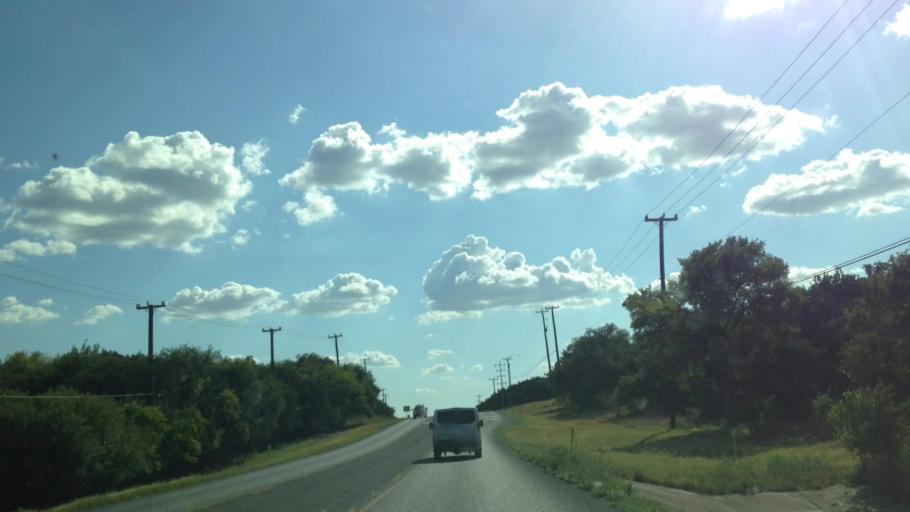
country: US
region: Texas
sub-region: Comal County
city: Garden Ridge
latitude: 29.6181
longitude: -98.3096
